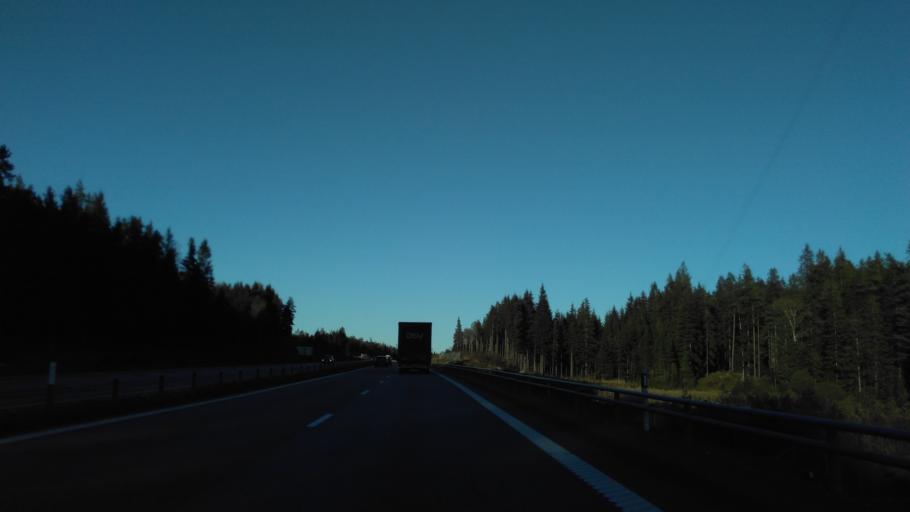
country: SE
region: Vaestra Goetaland
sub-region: Boras Kommun
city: Dalsjofors
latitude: 57.7457
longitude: 13.0663
